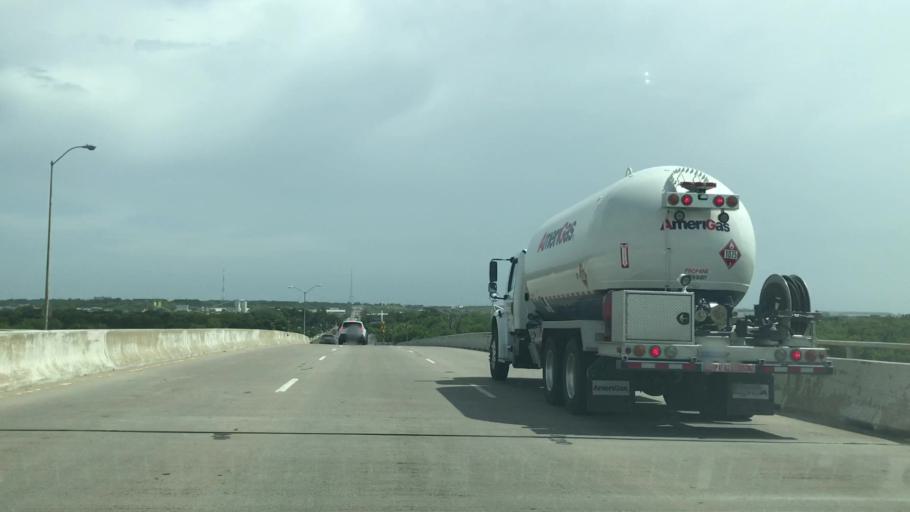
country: US
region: Texas
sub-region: Dallas County
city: Cockrell Hill
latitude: 32.7951
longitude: -96.8739
